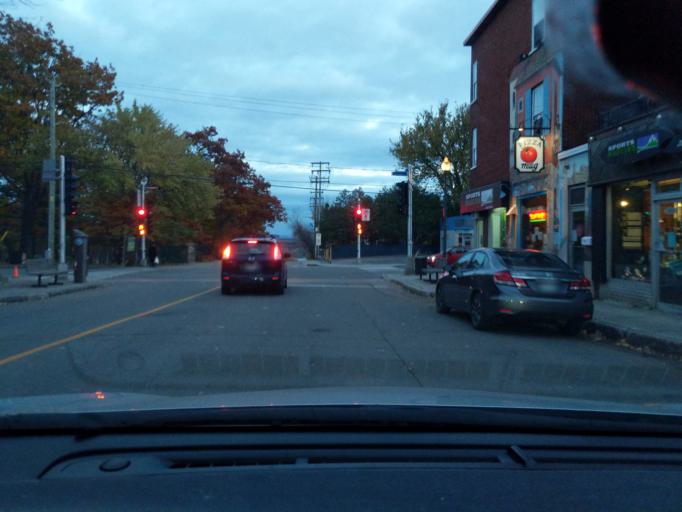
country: CA
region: Quebec
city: Quebec
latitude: 46.7795
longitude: -71.2498
